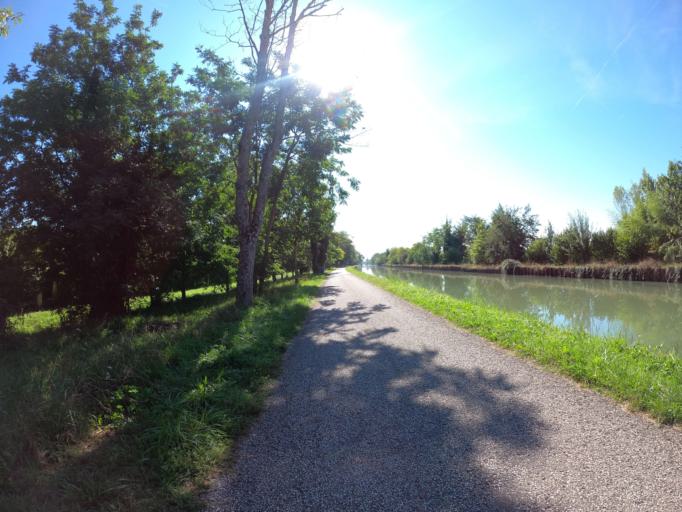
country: FR
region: Aquitaine
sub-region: Departement du Lot-et-Garonne
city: Bon-Encontre
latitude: 44.1831
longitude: 0.6584
